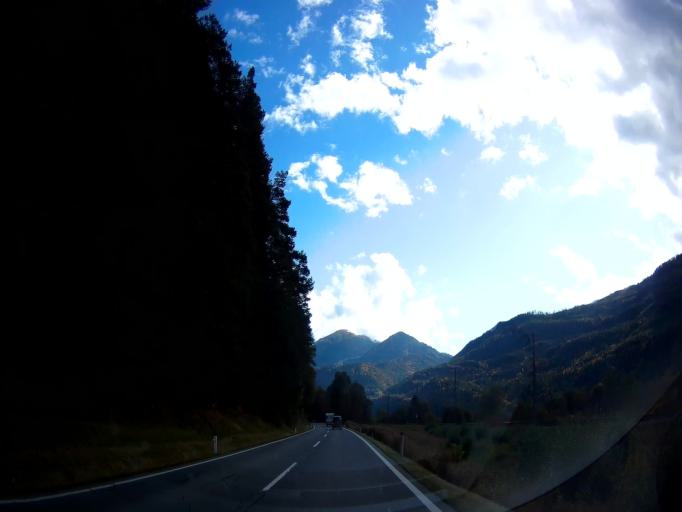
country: AT
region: Carinthia
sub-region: Politischer Bezirk Spittal an der Drau
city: Oberdrauburg
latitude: 46.7593
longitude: 12.9409
